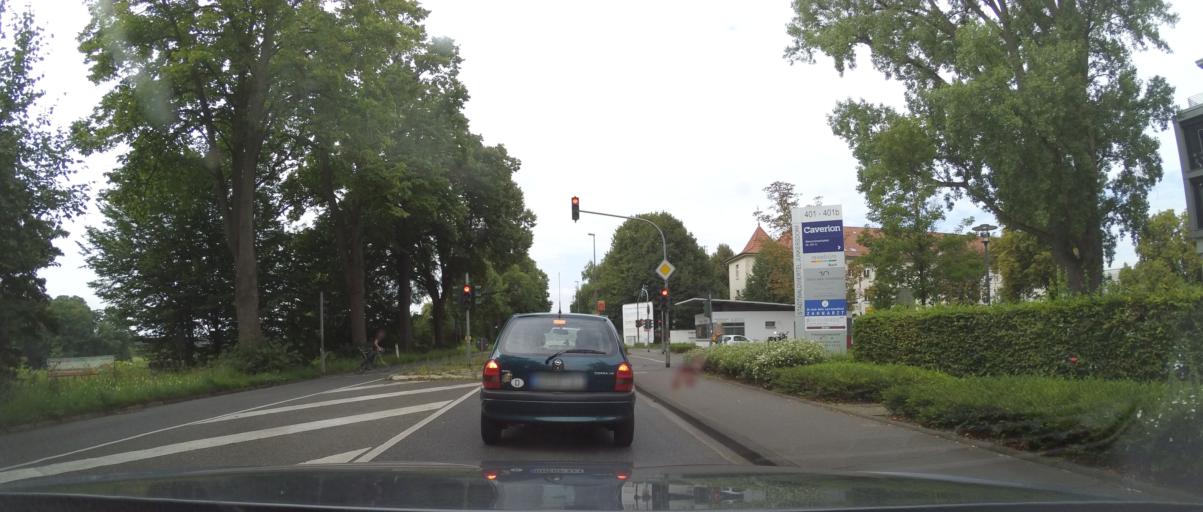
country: DE
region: North Rhine-Westphalia
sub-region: Regierungsbezirk Koln
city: Hurth
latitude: 50.9239
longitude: 6.8744
